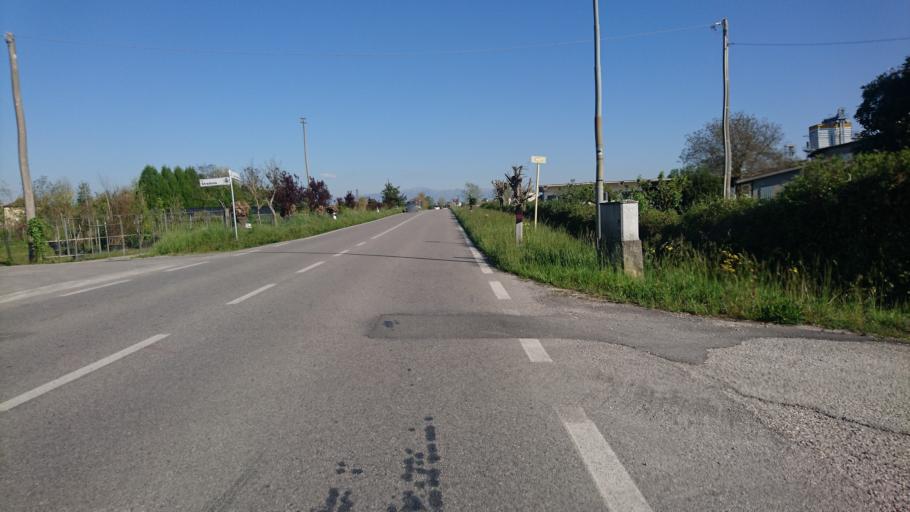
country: IT
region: Veneto
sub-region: Provincia di Padova
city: Piombino Dese
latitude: 45.5898
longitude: 12.0019
